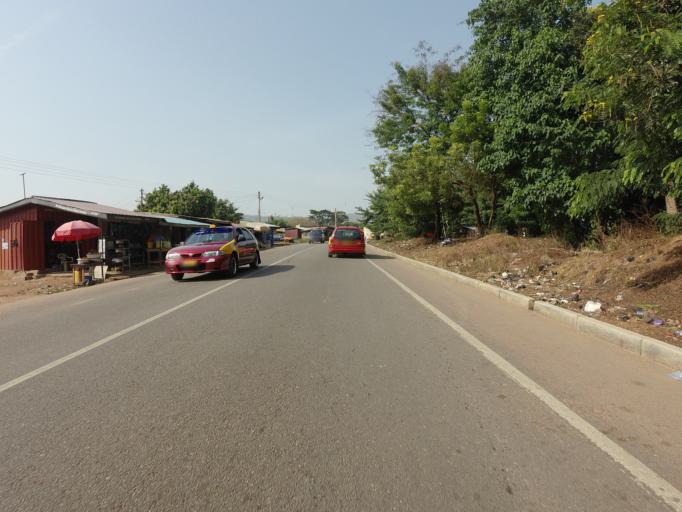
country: GH
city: Akropong
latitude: 6.1184
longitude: -0.0038
